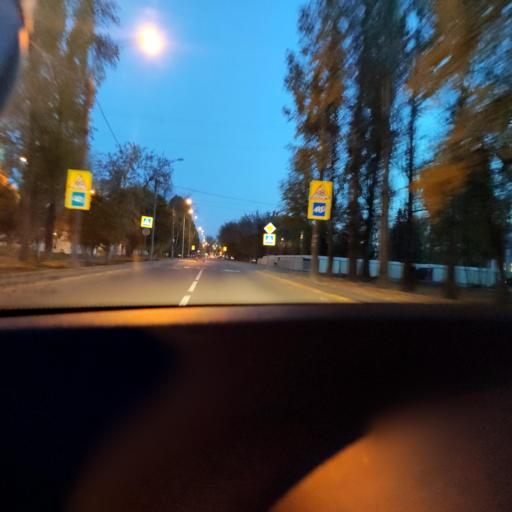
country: RU
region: Samara
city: Petra-Dubrava
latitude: 53.3022
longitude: 50.2831
